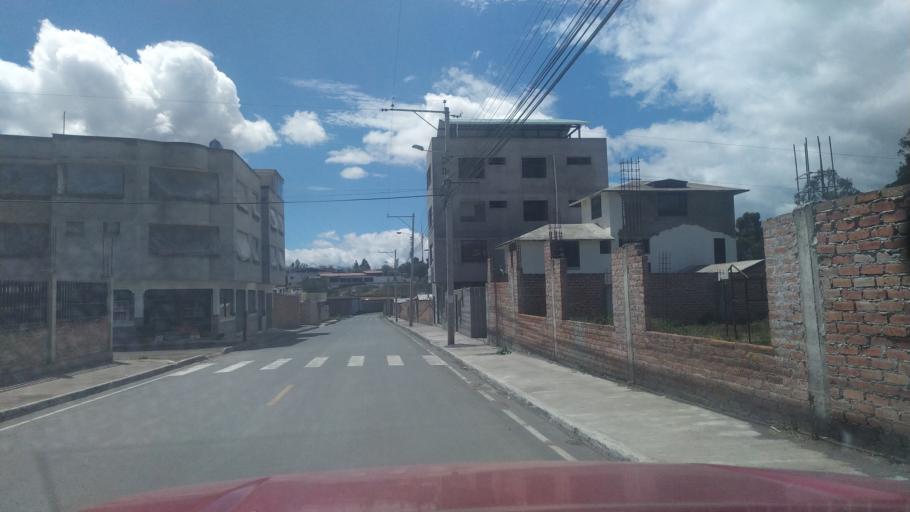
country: EC
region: Chimborazo
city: Riobamba
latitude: -1.6722
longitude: -78.6688
